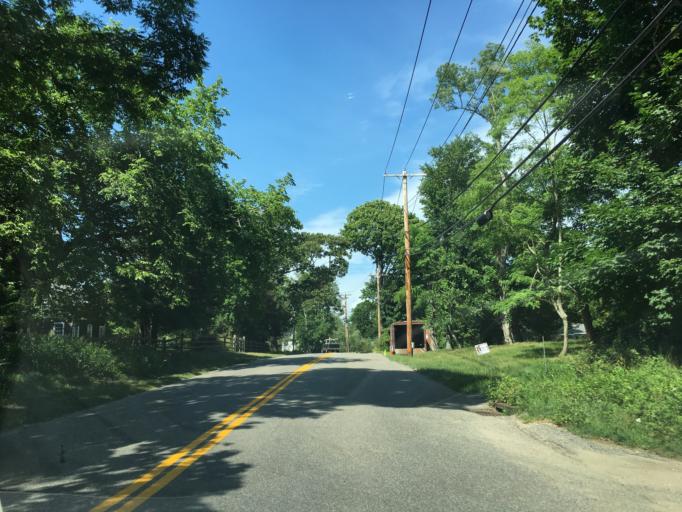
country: US
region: New York
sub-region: Suffolk County
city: Shelter Island Heights
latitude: 41.0723
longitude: -72.3593
